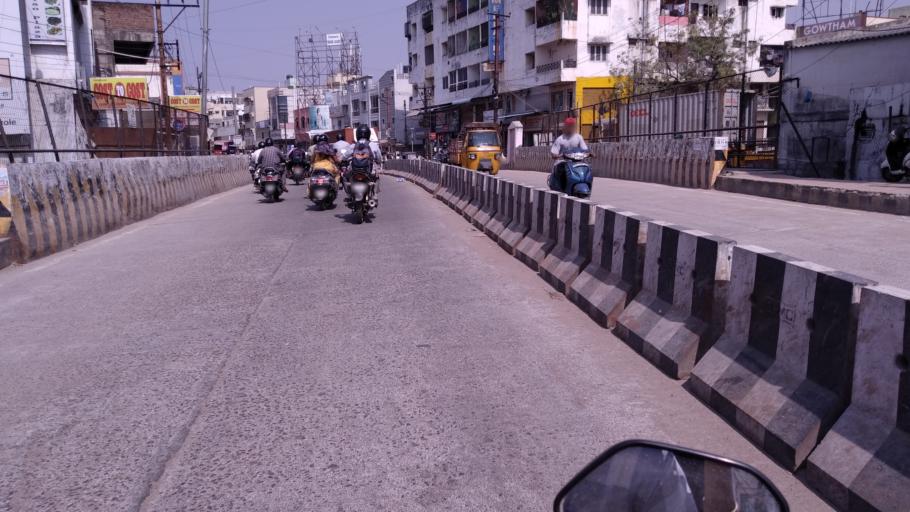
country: IN
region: Telangana
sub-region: Rangareddi
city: Quthbullapur
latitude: 17.4657
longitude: 78.4829
